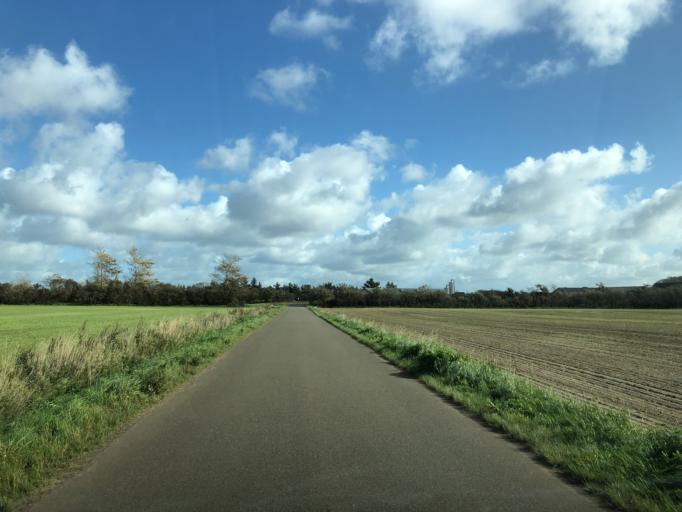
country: DK
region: Central Jutland
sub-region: Holstebro Kommune
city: Ulfborg
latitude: 56.2907
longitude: 8.3245
